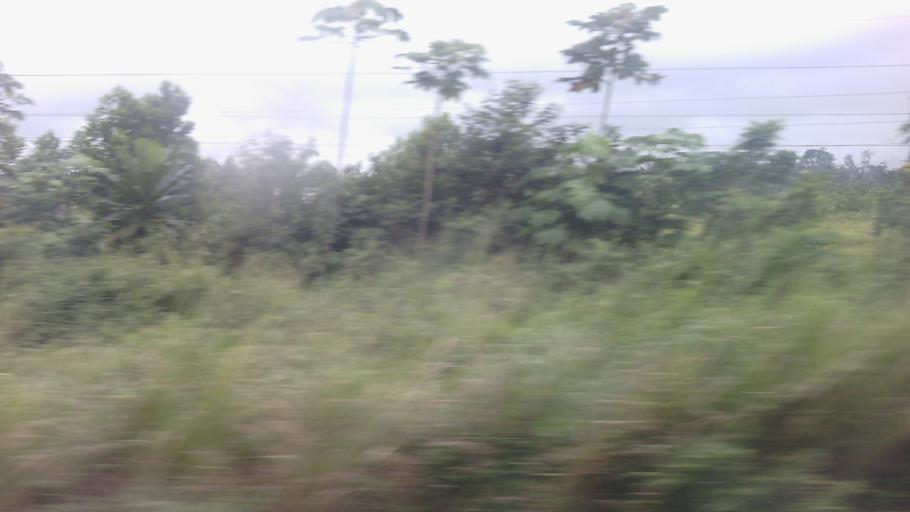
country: CI
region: Sud-Comoe
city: Aboisso
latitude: 5.4102
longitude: -3.2883
